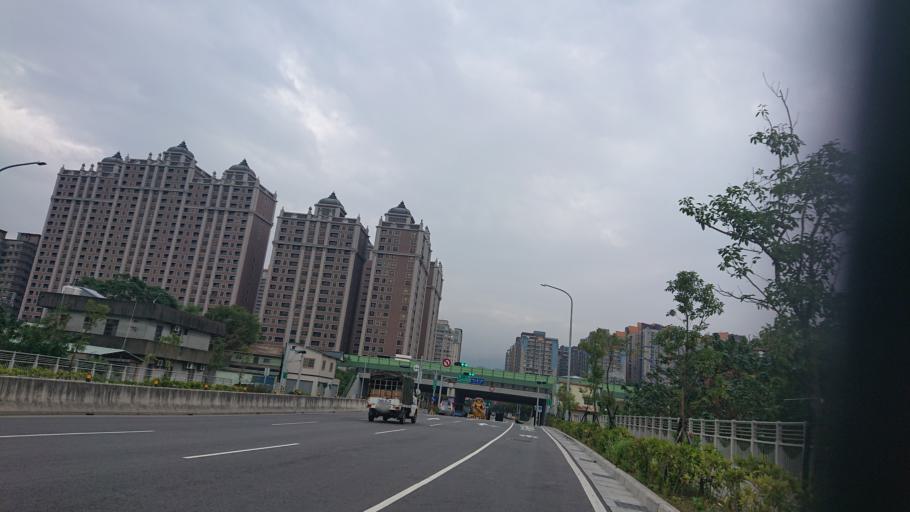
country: TW
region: Taiwan
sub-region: Taoyuan
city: Taoyuan
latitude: 24.9513
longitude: 121.3753
